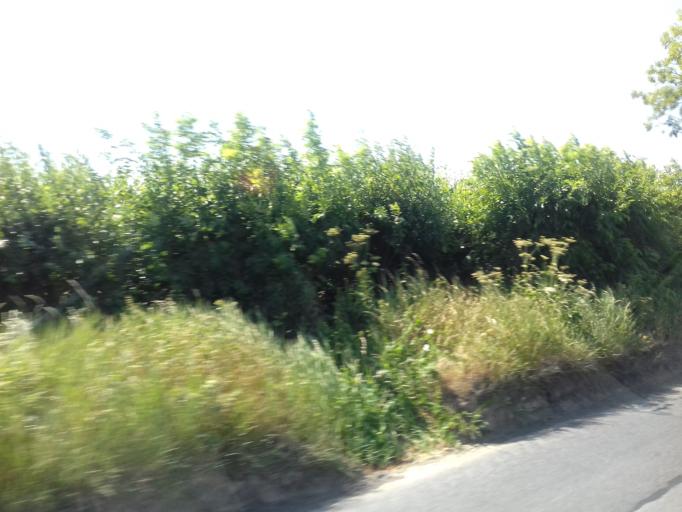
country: IE
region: Leinster
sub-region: Fingal County
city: Swords
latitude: 53.5177
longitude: -6.2538
